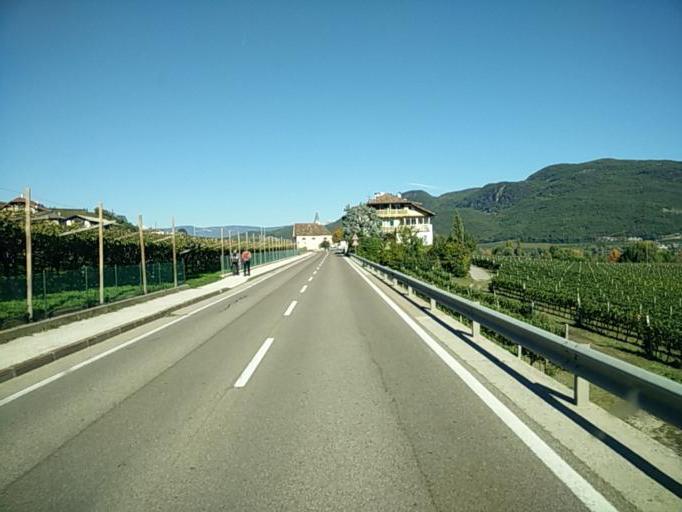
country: IT
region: Trentino-Alto Adige
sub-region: Bolzano
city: Termeno
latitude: 46.3743
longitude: 11.2514
